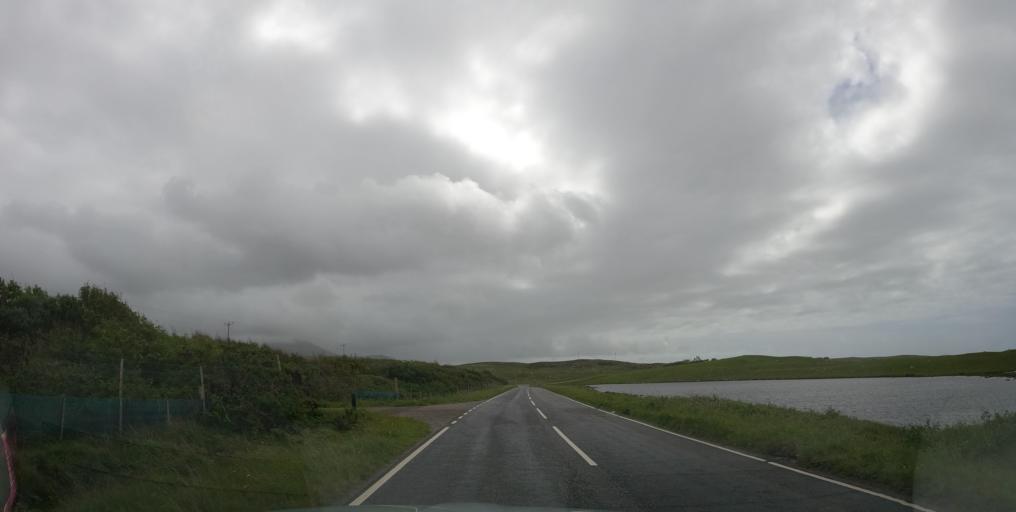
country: GB
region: Scotland
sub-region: Eilean Siar
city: Isle of South Uist
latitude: 57.2968
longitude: -7.3650
